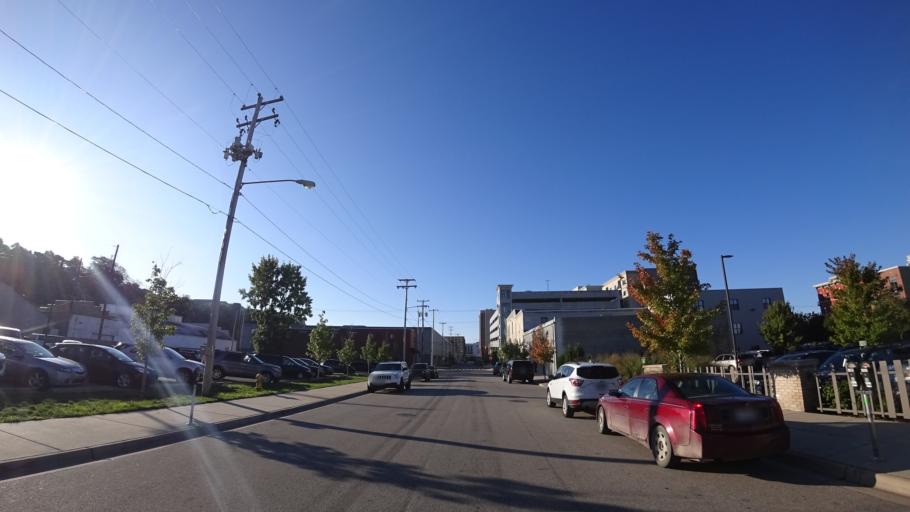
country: US
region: Michigan
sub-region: Kent County
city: Grand Rapids
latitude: 42.9775
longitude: -85.6714
